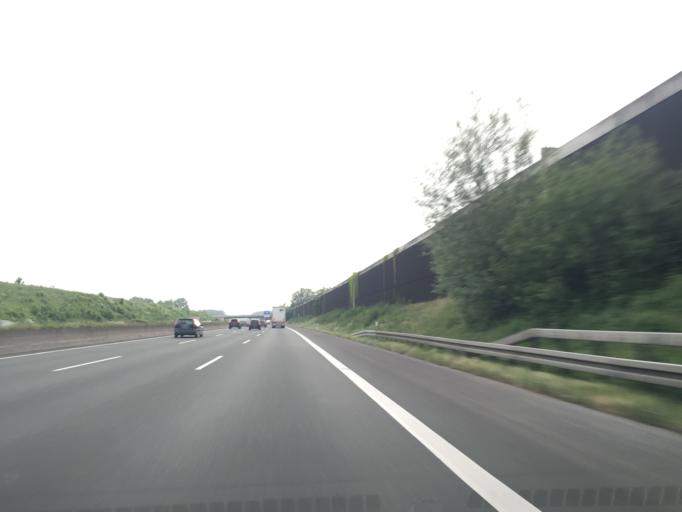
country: DE
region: North Rhine-Westphalia
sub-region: Regierungsbezirk Munster
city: Muenster
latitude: 51.9579
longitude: 7.5461
